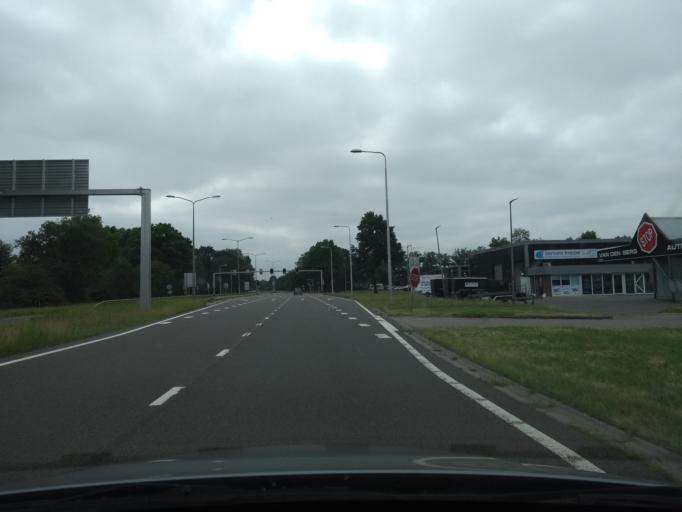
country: NL
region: Overijssel
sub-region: Gemeente Wierden
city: Wierden
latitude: 52.3527
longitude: 6.6244
